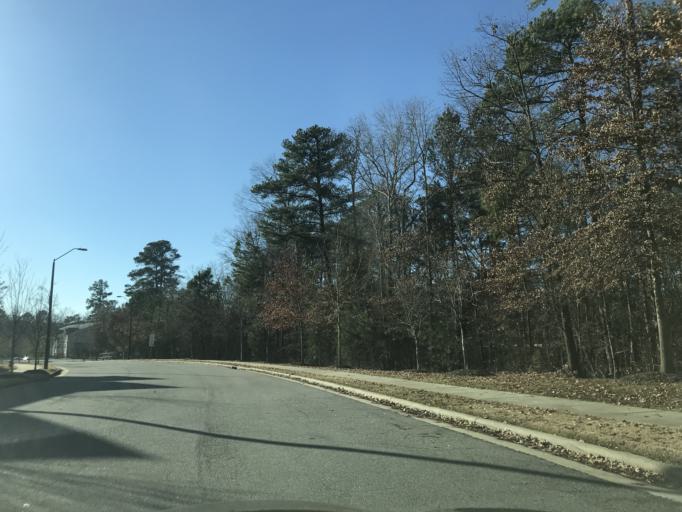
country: US
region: North Carolina
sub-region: Wake County
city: Morrisville
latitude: 35.8999
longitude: -78.8061
